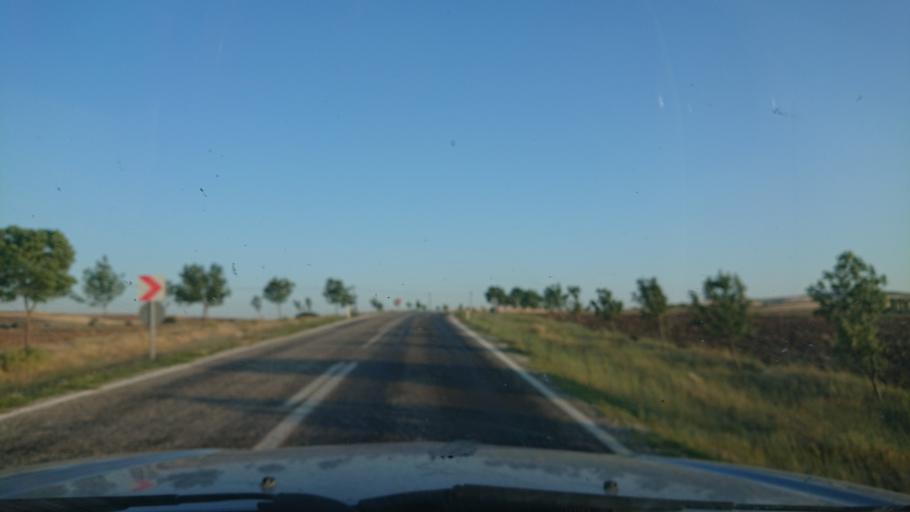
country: TR
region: Aksaray
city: Sariyahsi
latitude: 38.9502
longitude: 33.8388
